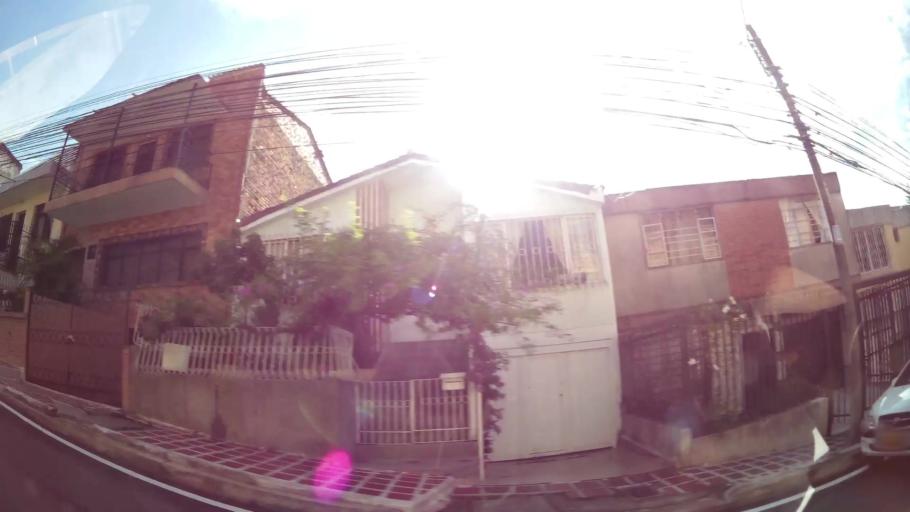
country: CO
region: Valle del Cauca
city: Cali
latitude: 3.4397
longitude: -76.5398
